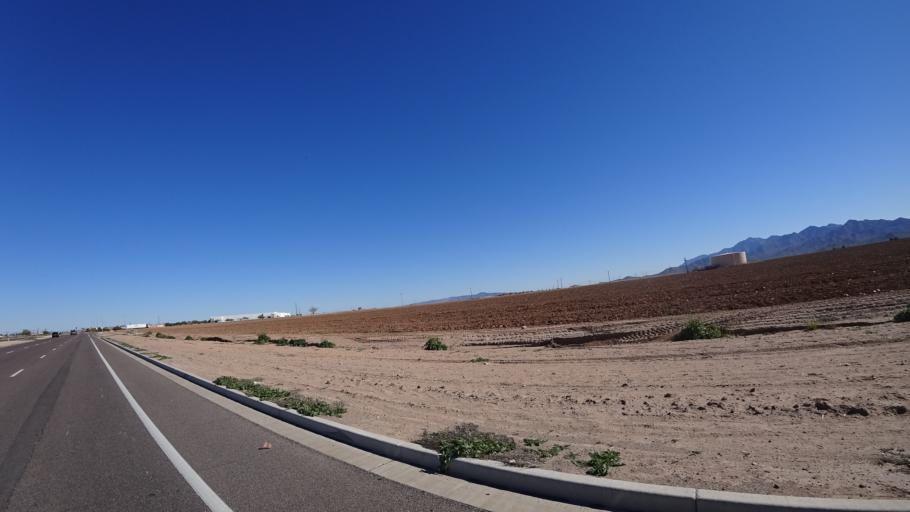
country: US
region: Arizona
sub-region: Maricopa County
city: Goodyear
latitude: 33.4177
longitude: -112.3700
